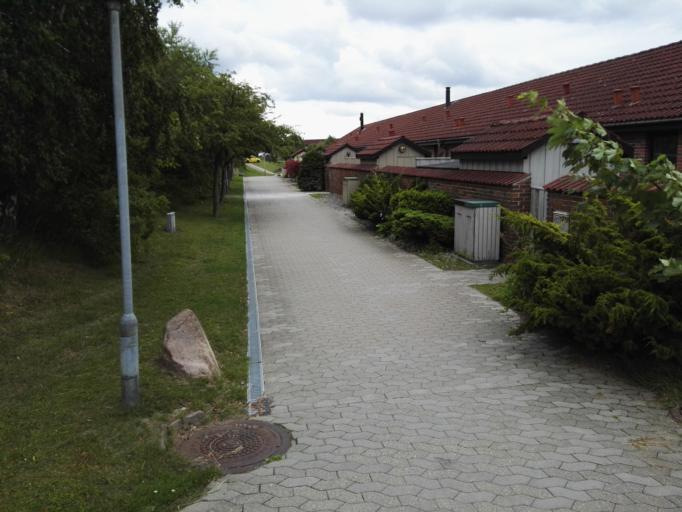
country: DK
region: Capital Region
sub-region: Egedal Kommune
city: Vekso
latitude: 55.7567
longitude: 12.2313
